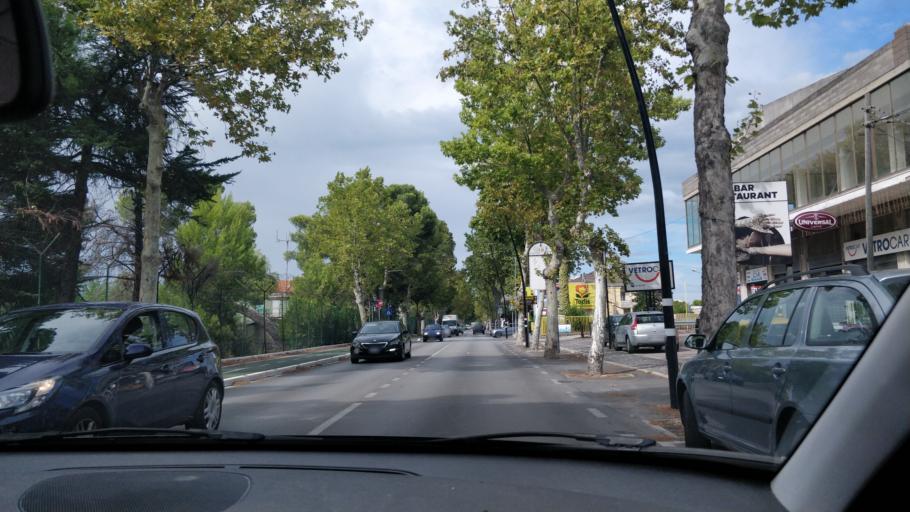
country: IT
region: Abruzzo
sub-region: Provincia di Chieti
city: Sambuceto
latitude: 42.4333
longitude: 14.1915
